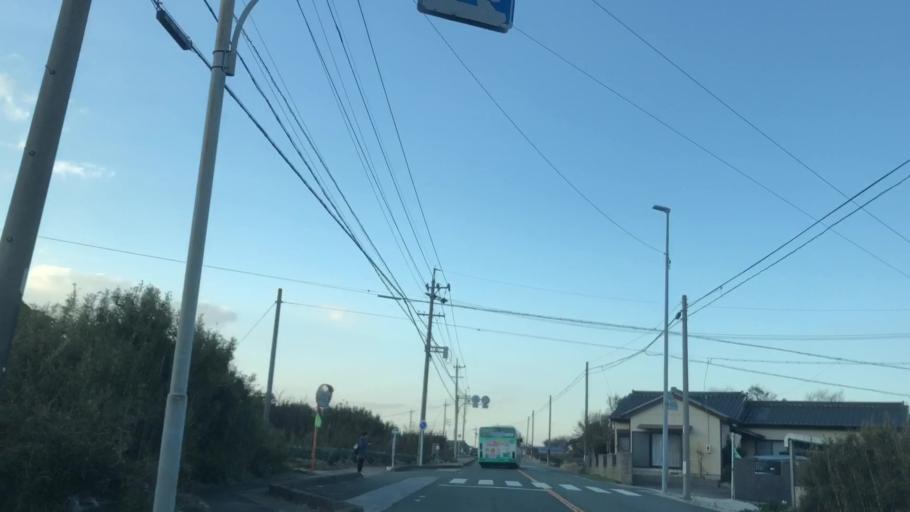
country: JP
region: Aichi
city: Tahara
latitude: 34.6630
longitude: 137.1956
